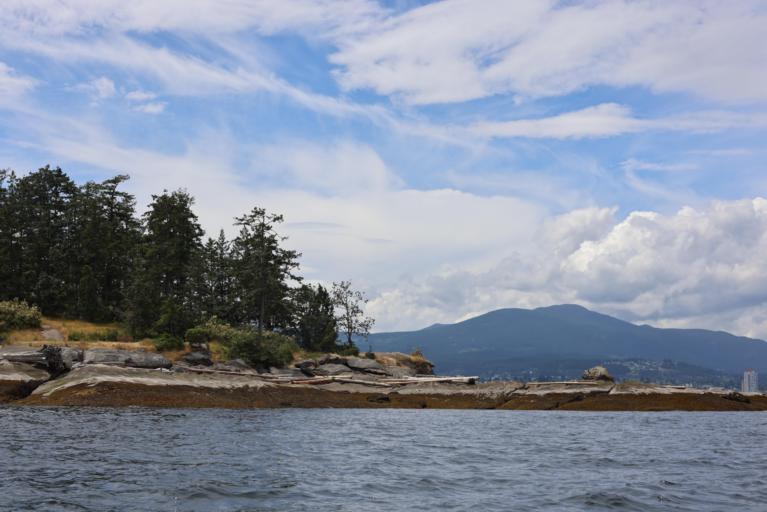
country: CA
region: British Columbia
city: Nanaimo
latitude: 49.1677
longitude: -123.8931
